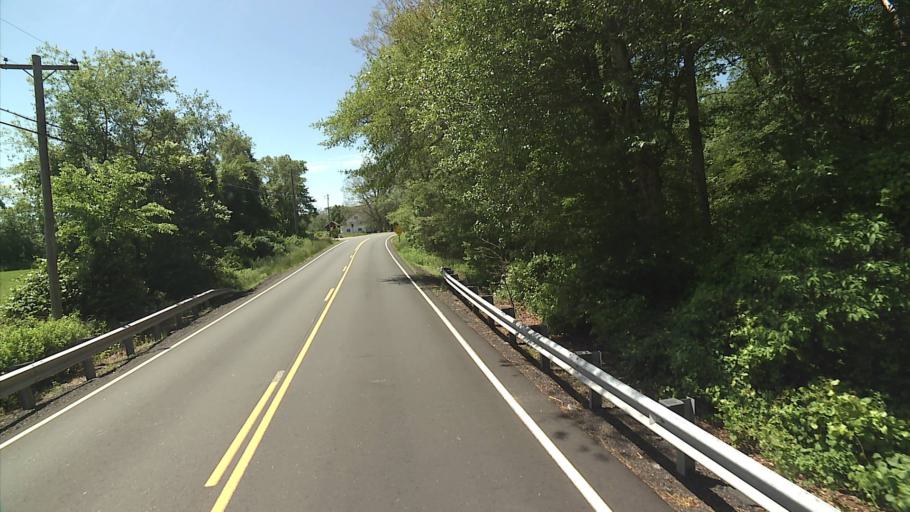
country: US
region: Connecticut
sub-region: Windham County
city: Plainfield
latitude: 41.6097
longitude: -71.8427
